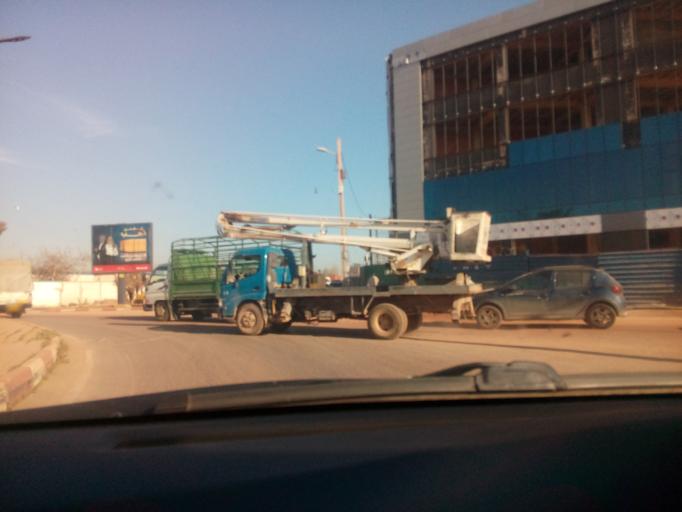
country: DZ
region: Oran
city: Es Senia
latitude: 35.6489
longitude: -0.6118
